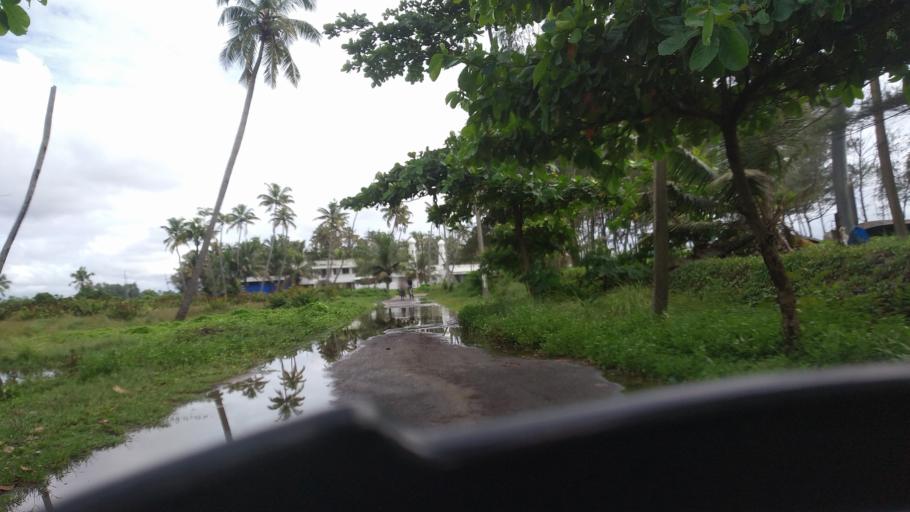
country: IN
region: Kerala
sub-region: Ernakulam
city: Elur
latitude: 10.0995
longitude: 76.1899
